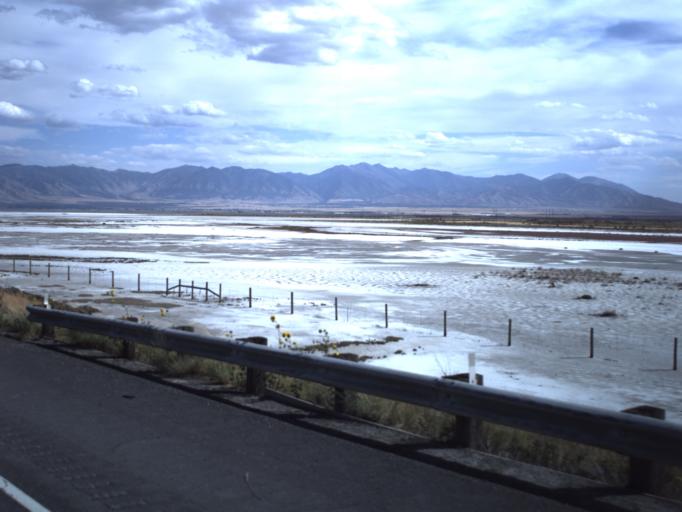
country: US
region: Utah
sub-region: Tooele County
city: Grantsville
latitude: 40.6831
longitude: -112.4367
